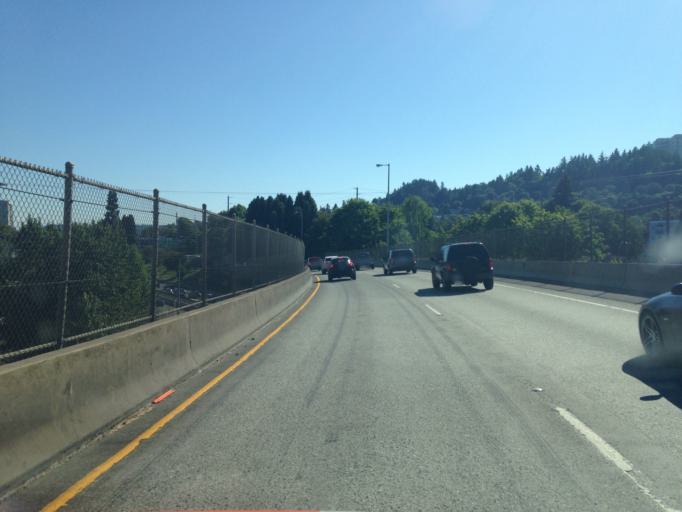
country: US
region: Oregon
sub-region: Multnomah County
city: Portland
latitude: 45.5046
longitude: -122.6743
